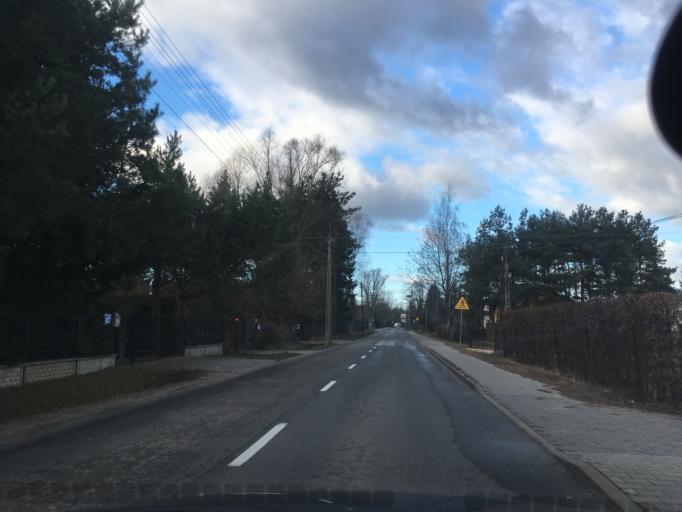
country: PL
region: Masovian Voivodeship
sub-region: Powiat piaseczynski
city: Lesznowola
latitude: 52.0345
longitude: 20.9490
